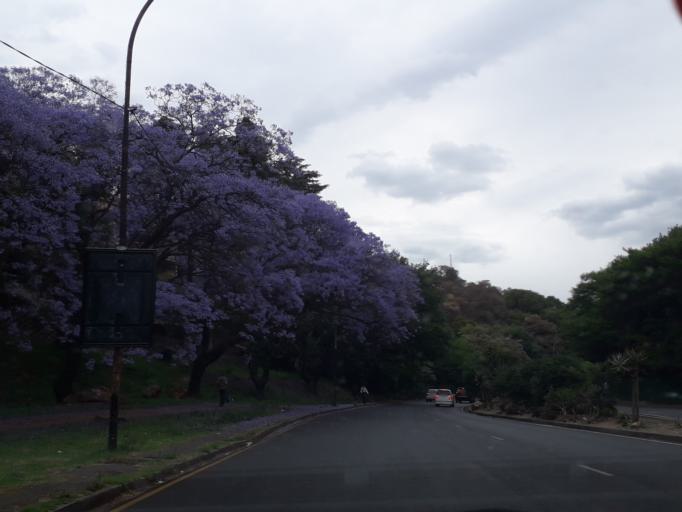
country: ZA
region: Gauteng
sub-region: City of Johannesburg Metropolitan Municipality
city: Johannesburg
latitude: -26.1720
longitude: 28.0537
